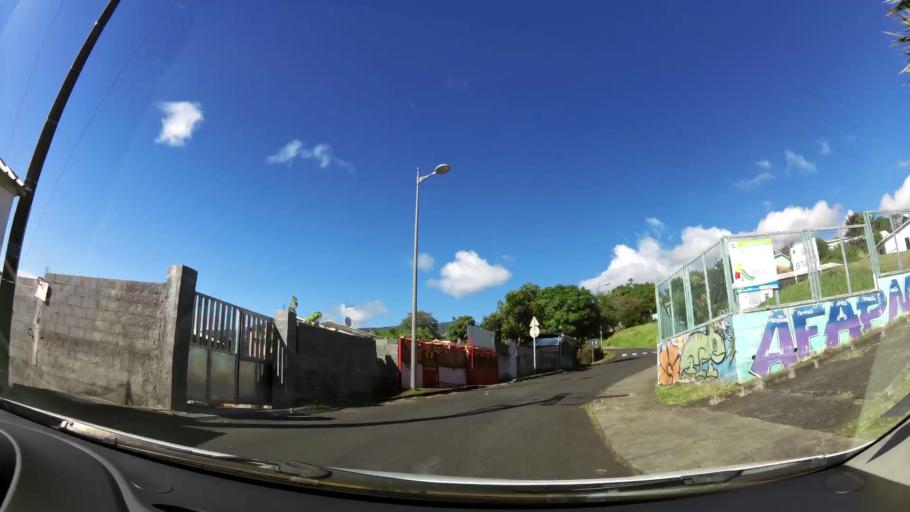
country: RE
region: Reunion
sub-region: Reunion
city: Saint-Denis
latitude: -20.9162
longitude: 55.4867
